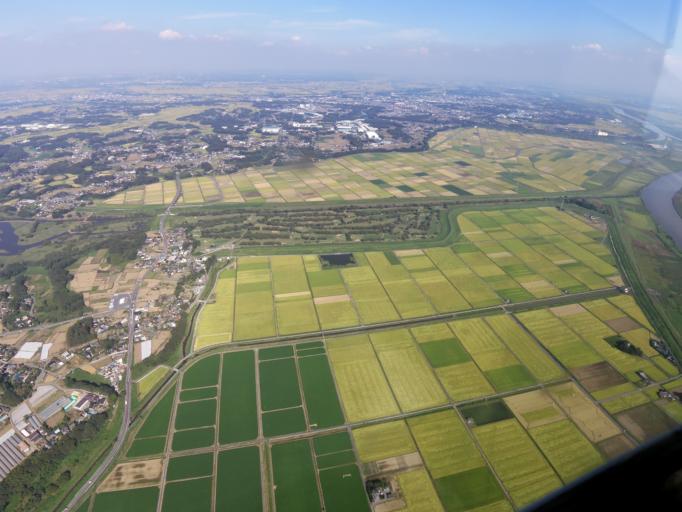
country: JP
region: Ibaraki
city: Iwai
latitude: 35.9858
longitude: 139.9059
